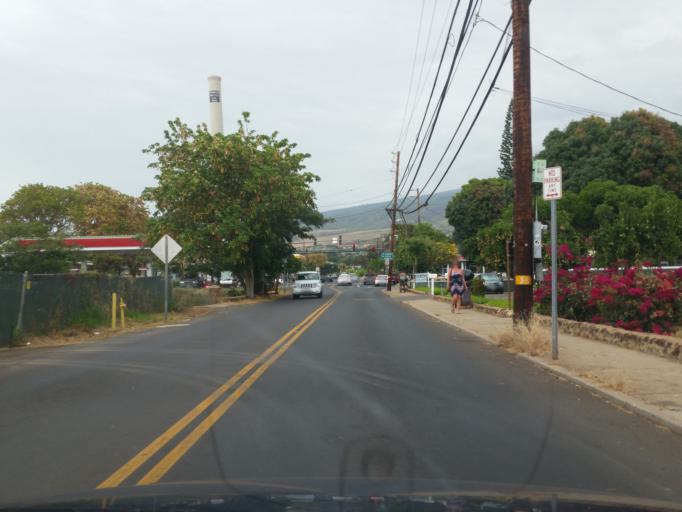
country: US
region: Hawaii
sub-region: Maui County
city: Lahaina
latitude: 20.8768
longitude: -156.6779
